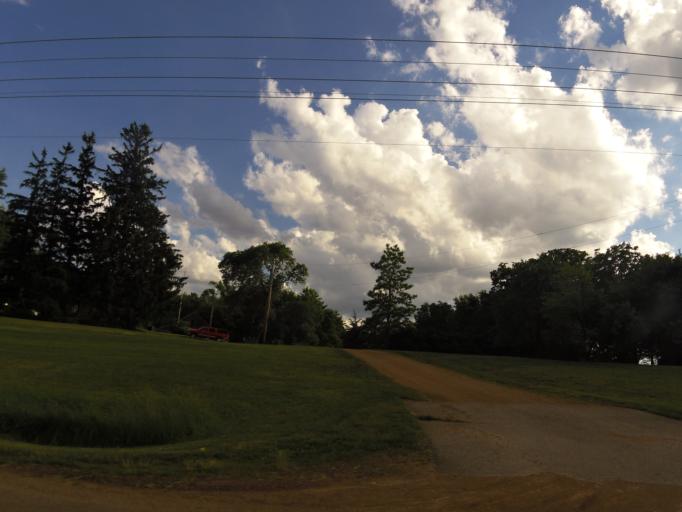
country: US
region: Minnesota
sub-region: Carver County
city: Waconia
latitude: 44.8191
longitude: -93.7299
